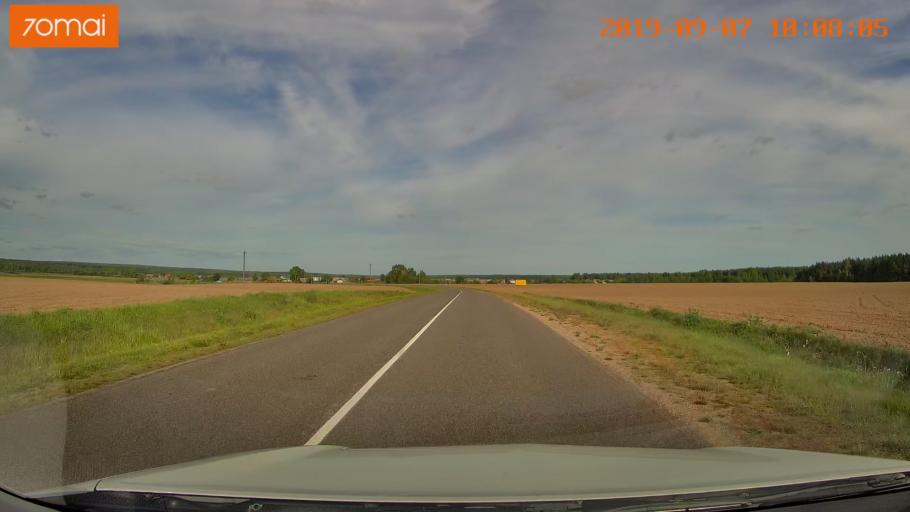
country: BY
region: Grodnenskaya
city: Voranava
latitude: 54.0836
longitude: 25.3922
